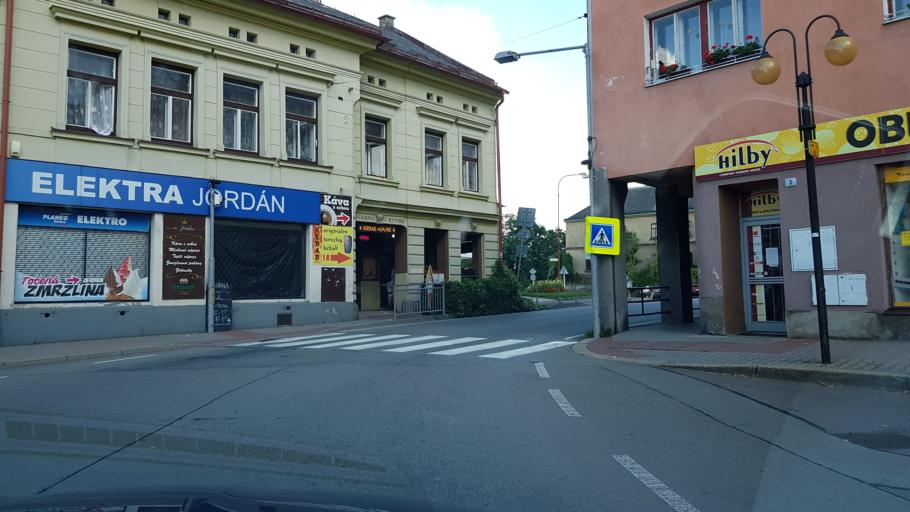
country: CZ
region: Pardubicky
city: Zamberk
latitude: 50.0872
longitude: 16.4656
